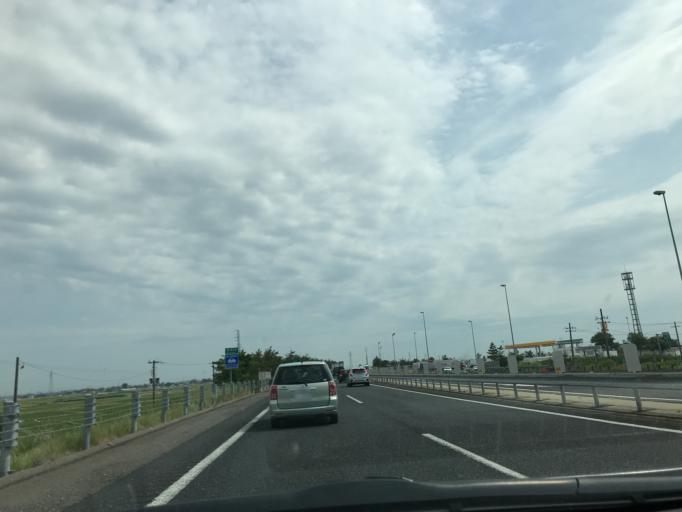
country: JP
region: Niigata
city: Shirone
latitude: 37.8153
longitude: 138.9752
